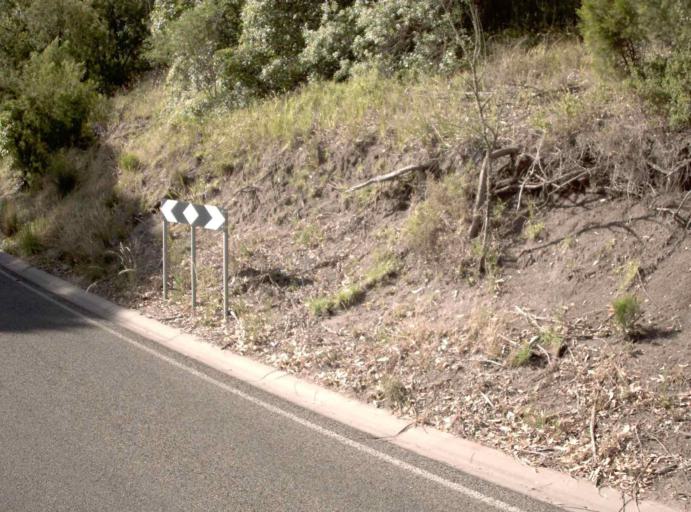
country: AU
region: Victoria
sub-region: East Gippsland
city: Lakes Entrance
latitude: -37.8787
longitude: 147.8578
